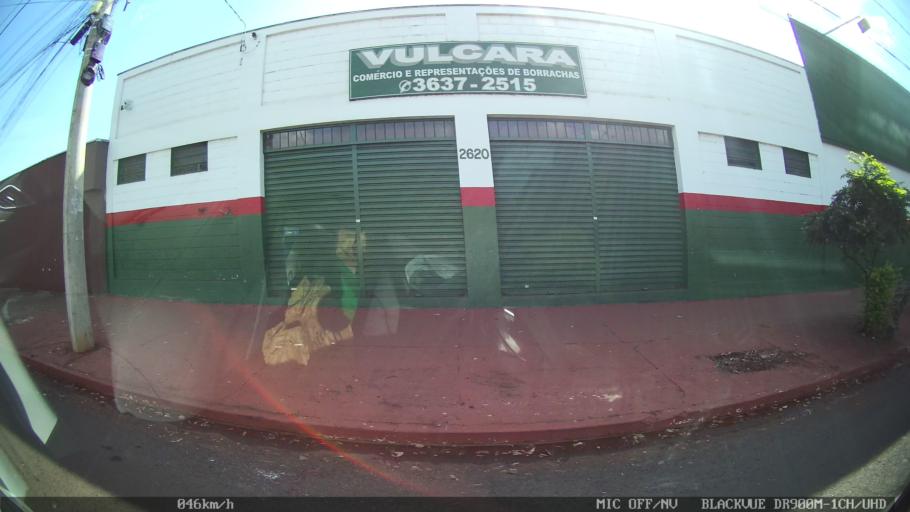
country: BR
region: Sao Paulo
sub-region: Ribeirao Preto
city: Ribeirao Preto
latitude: -21.1863
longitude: -47.8433
